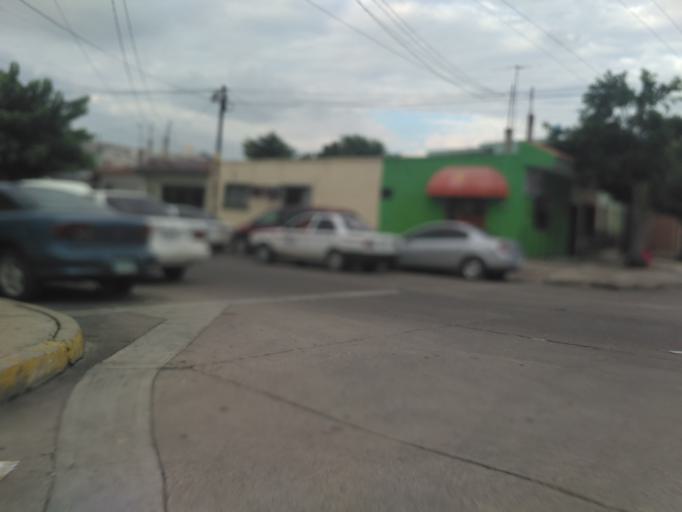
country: MX
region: Sinaloa
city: Culiacan
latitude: 24.7981
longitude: -107.3975
